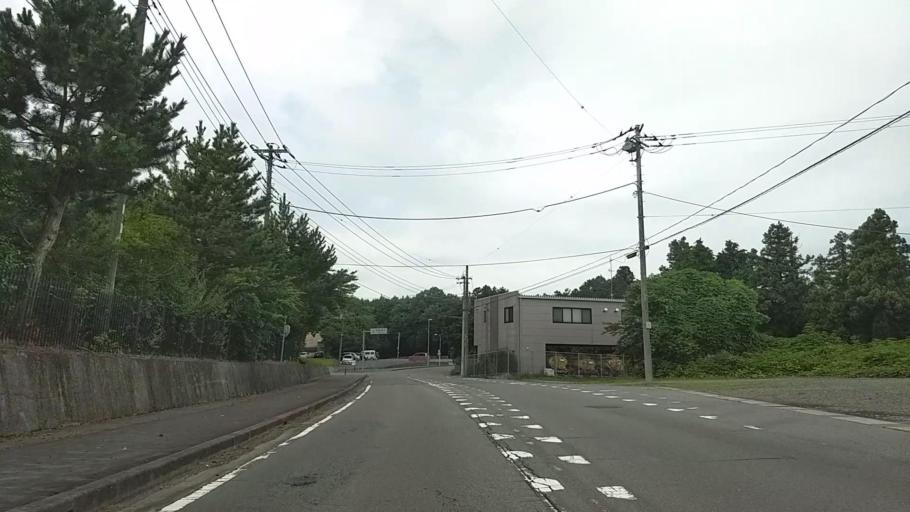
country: JP
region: Shizuoka
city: Gotemba
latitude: 35.3247
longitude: 138.9713
